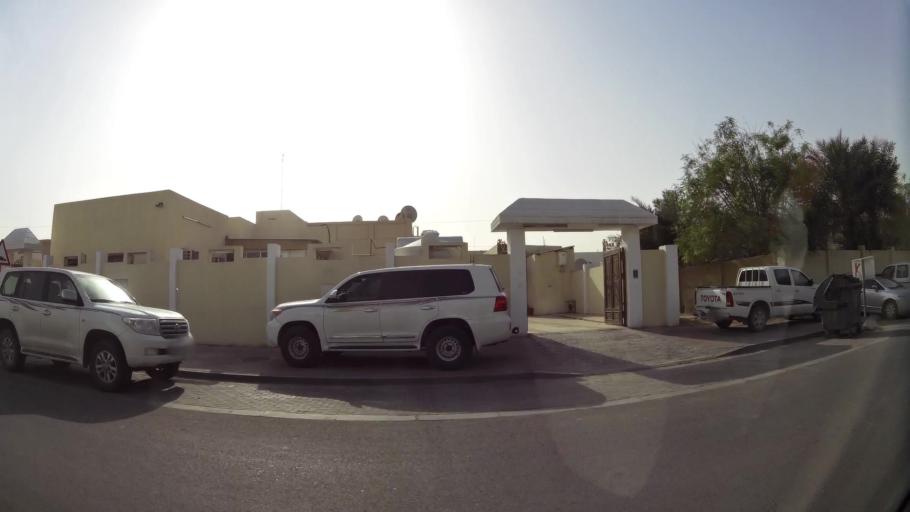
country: QA
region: Baladiyat ar Rayyan
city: Ar Rayyan
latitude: 25.2347
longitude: 51.4367
